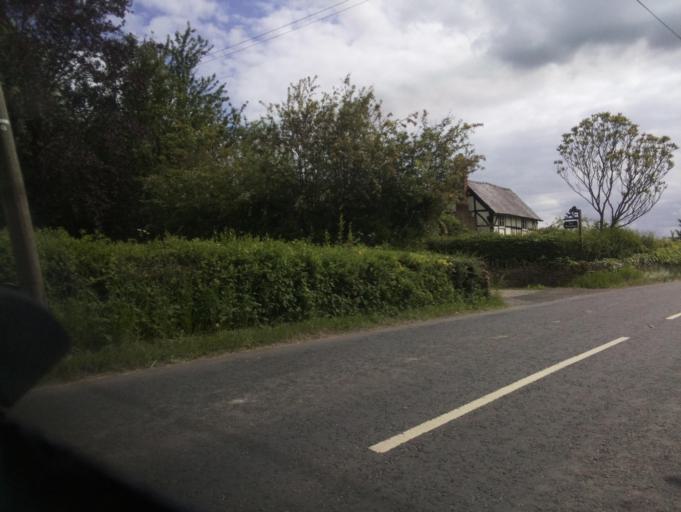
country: GB
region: England
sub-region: Herefordshire
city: Evesbatch
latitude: 52.1008
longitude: -2.4176
